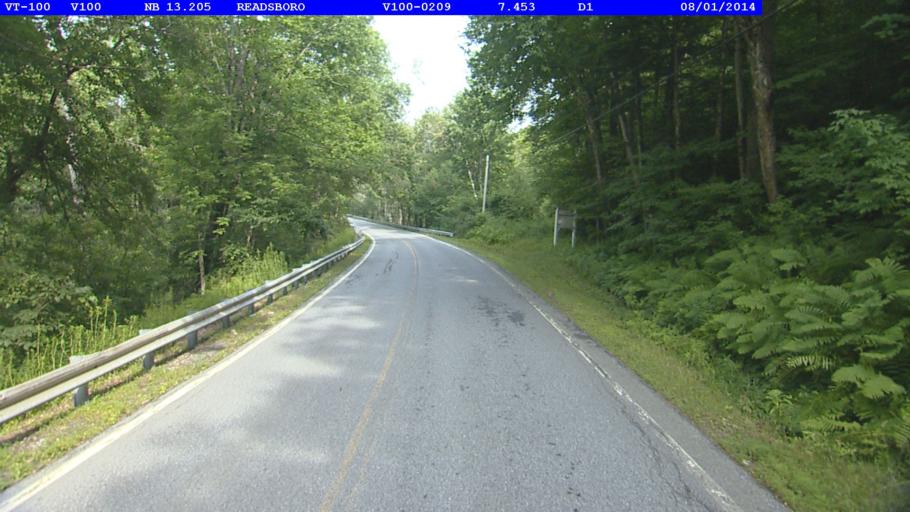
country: US
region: Massachusetts
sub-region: Franklin County
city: Charlemont
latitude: 42.7702
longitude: -72.9399
